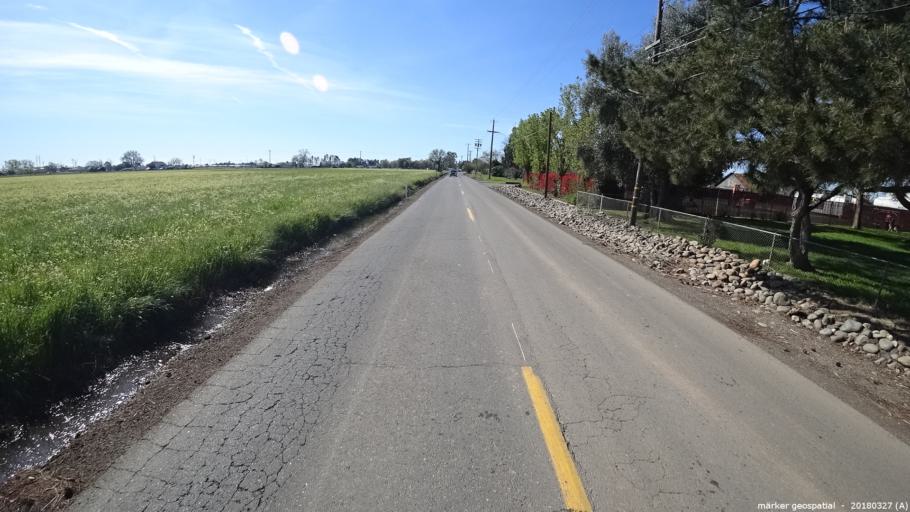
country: US
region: California
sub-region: Sacramento County
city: Vineyard
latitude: 38.4986
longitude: -121.3627
